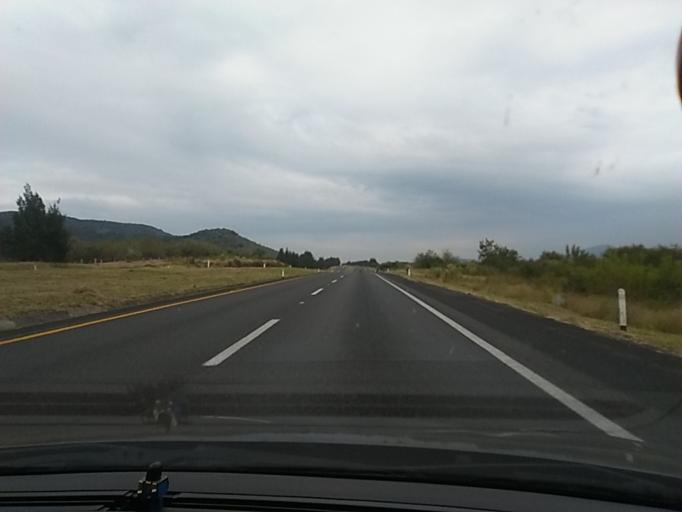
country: MX
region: Michoacan
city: Churintzio
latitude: 20.1046
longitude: -102.0335
